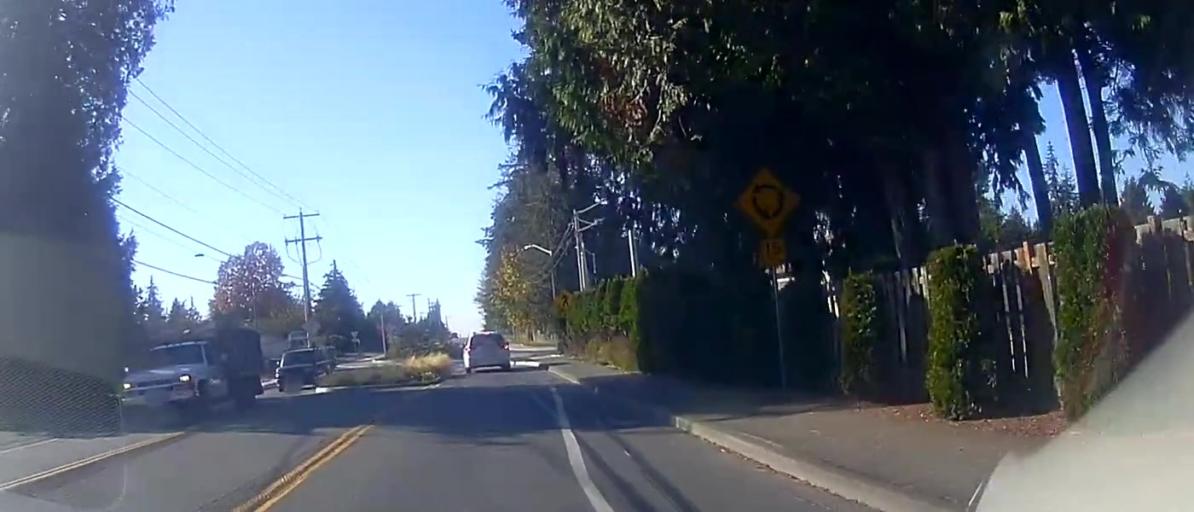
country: US
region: Washington
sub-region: Skagit County
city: Big Lake
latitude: 48.4200
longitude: -122.2860
